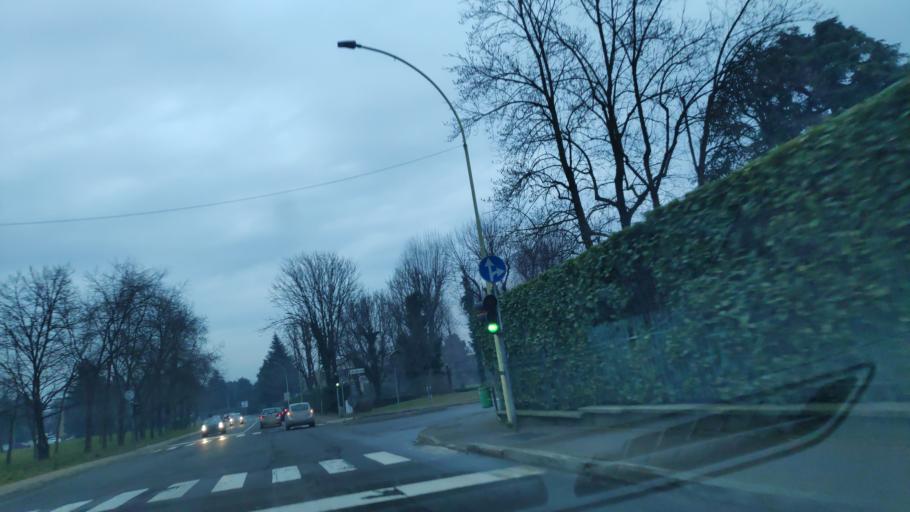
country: IT
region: Lombardy
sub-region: Citta metropolitana di Milano
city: Romano Banco
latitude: 45.4234
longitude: 9.1228
